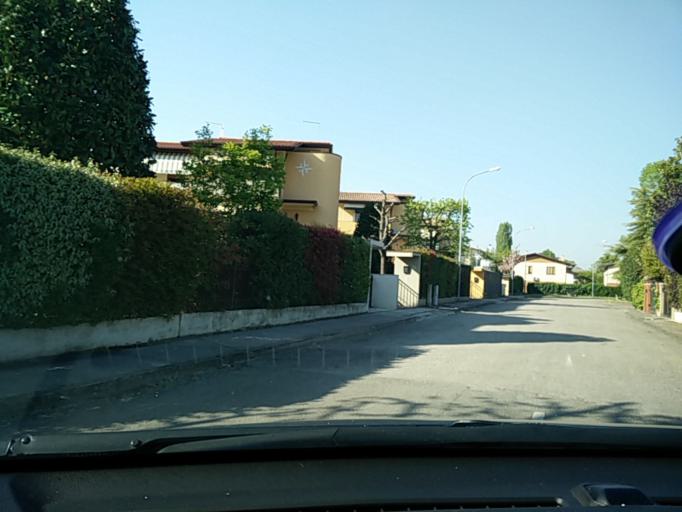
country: IT
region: Veneto
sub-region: Provincia di Venezia
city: Musile di Piave
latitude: 45.6185
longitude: 12.5591
